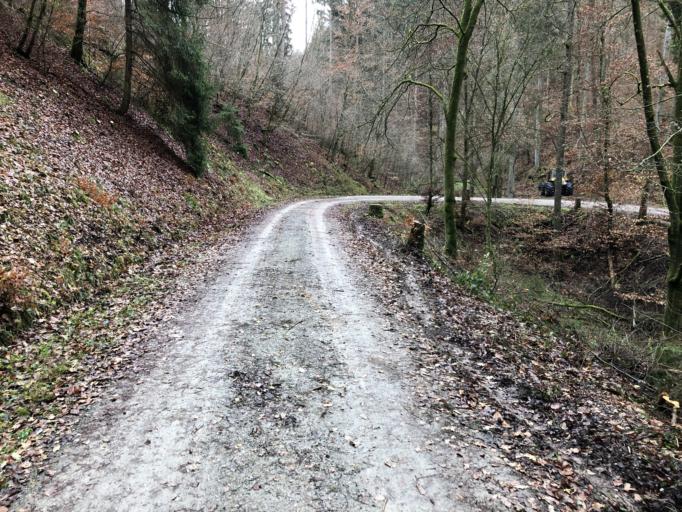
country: DE
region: Baden-Wuerttemberg
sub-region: Tuebingen Region
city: Tuebingen
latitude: 48.5545
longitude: 9.0082
